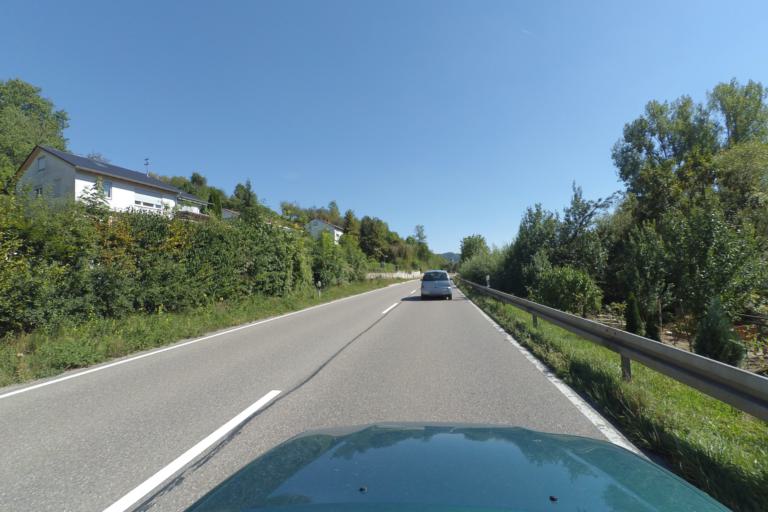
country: DE
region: Baden-Wuerttemberg
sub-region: Regierungsbezirk Stuttgart
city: Ingelfingen
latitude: 49.3038
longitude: 9.6390
